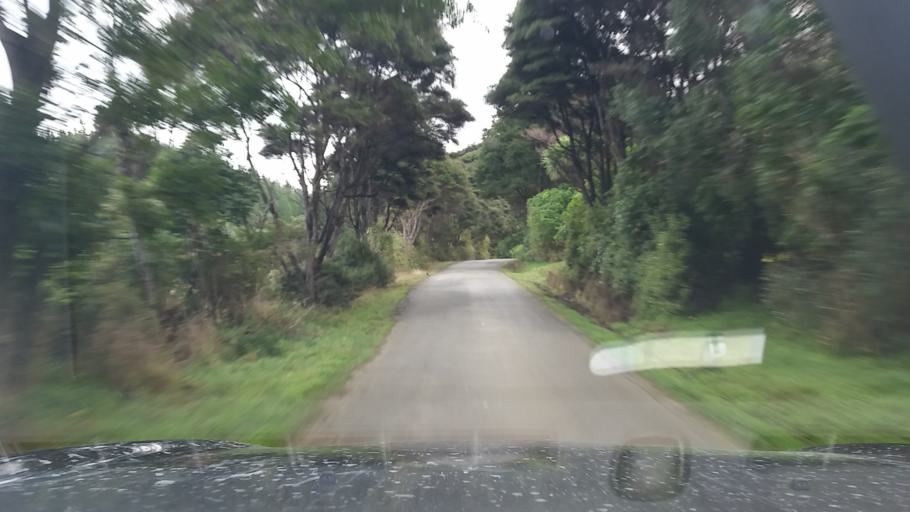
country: NZ
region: Marlborough
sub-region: Marlborough District
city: Picton
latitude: -41.1757
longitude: 174.0598
